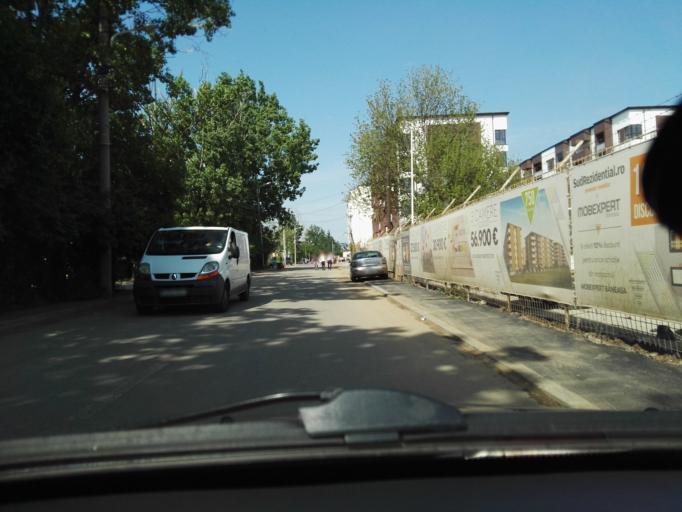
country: RO
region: Ilfov
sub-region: Comuna Popesti-Leordeni
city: Popesti-Leordeni
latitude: 44.3730
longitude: 26.1253
